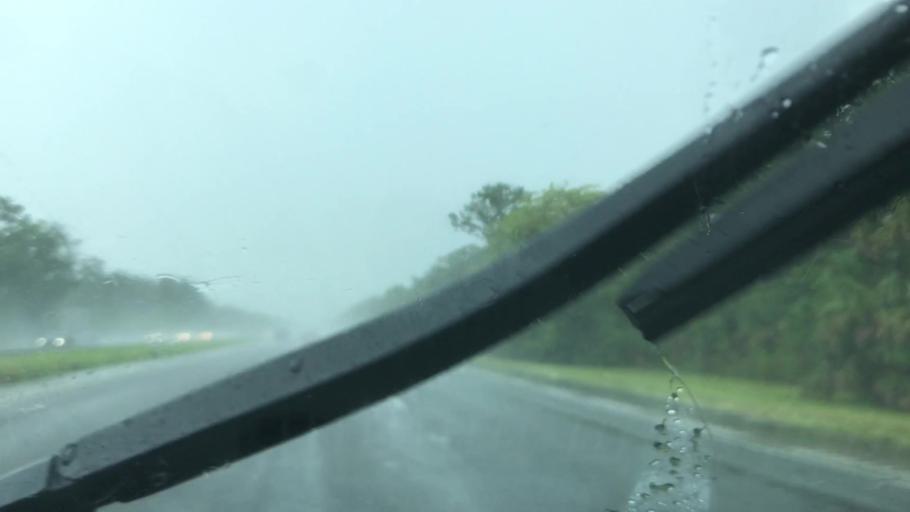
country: US
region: Florida
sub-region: Flagler County
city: Flagler Beach
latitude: 29.3904
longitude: -81.1495
